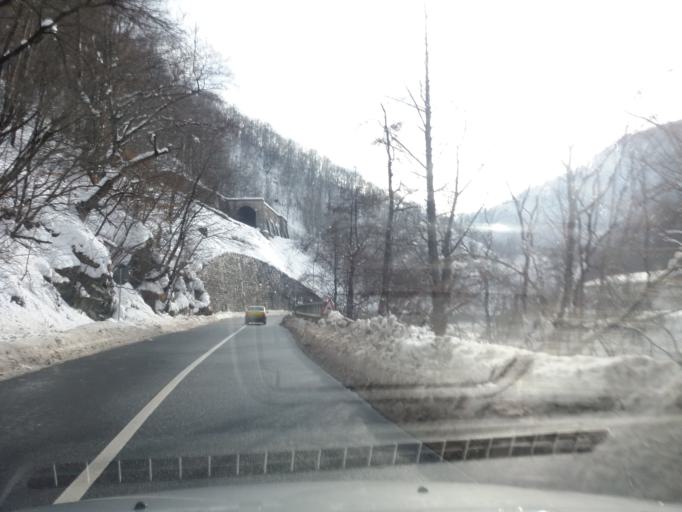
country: RO
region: Hunedoara
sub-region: Comuna Aninoasa
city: Iscroni
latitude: 45.2943
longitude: 23.3831
